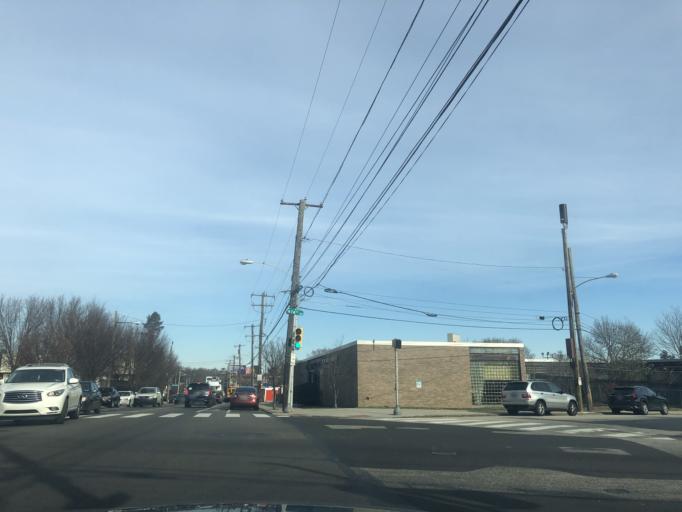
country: US
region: Pennsylvania
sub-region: Montgomery County
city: Wyncote
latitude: 40.0668
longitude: -75.1583
